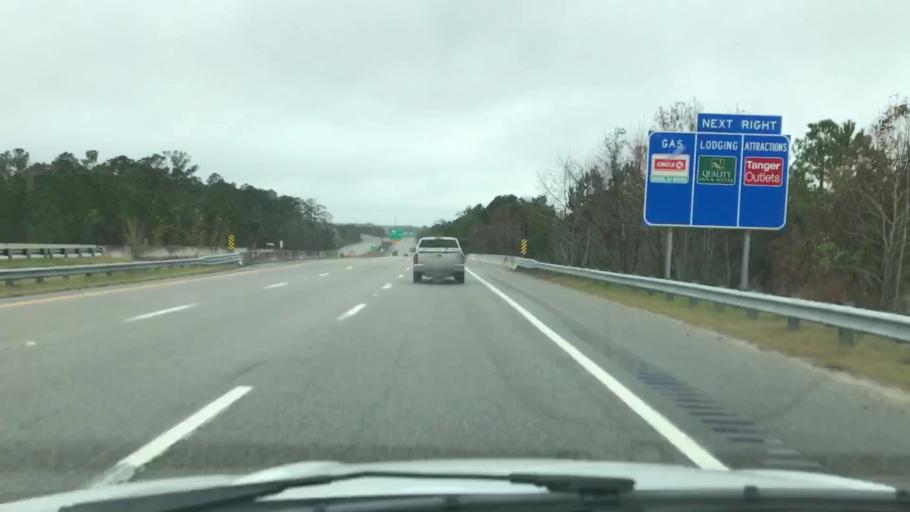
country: US
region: South Carolina
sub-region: Horry County
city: Forestbrook
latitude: 33.7426
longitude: -78.9384
